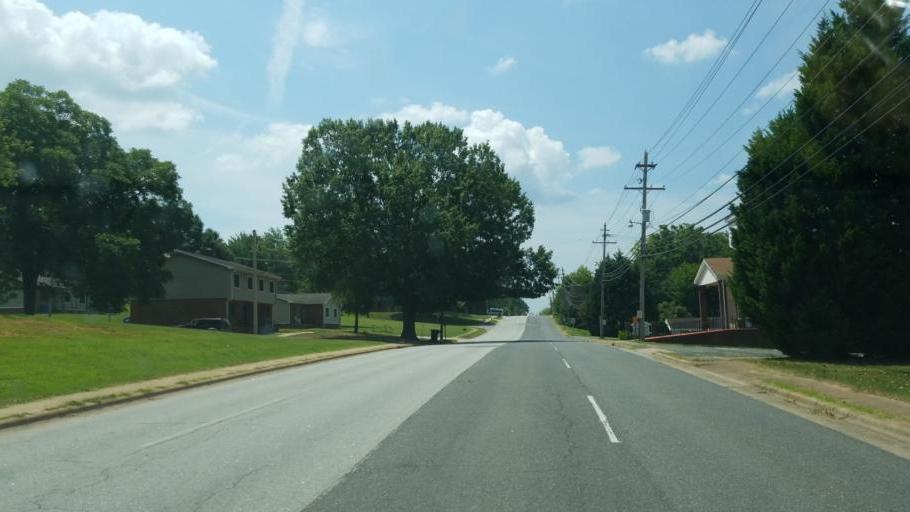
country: US
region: North Carolina
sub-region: Cleveland County
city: Kings Mountain
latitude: 35.2439
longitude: -81.3467
